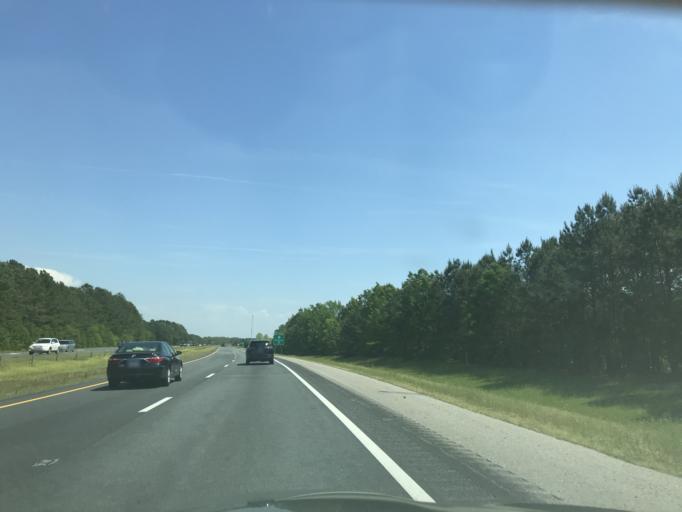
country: US
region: North Carolina
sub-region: Johnston County
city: Benson
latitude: 35.3317
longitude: -78.4560
